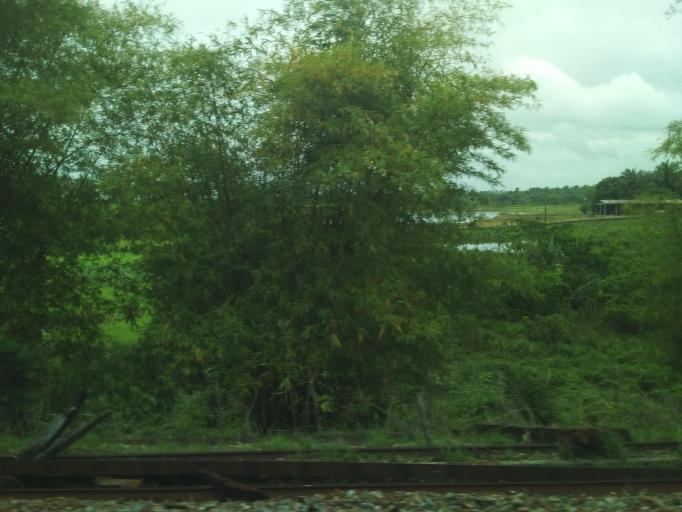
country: BR
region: Maranhao
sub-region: Vitoria Do Mearim
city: Vitoria do Mearim
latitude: -3.5342
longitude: -44.8798
